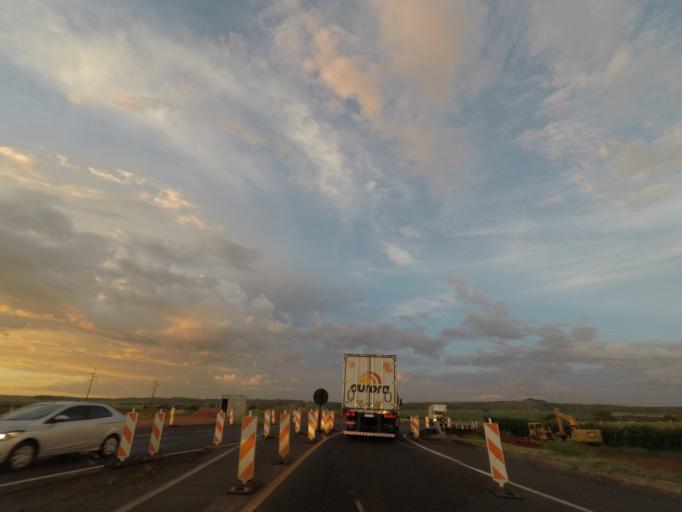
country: BR
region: Minas Gerais
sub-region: Uberaba
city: Uberaba
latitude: -19.6268
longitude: -48.0150
